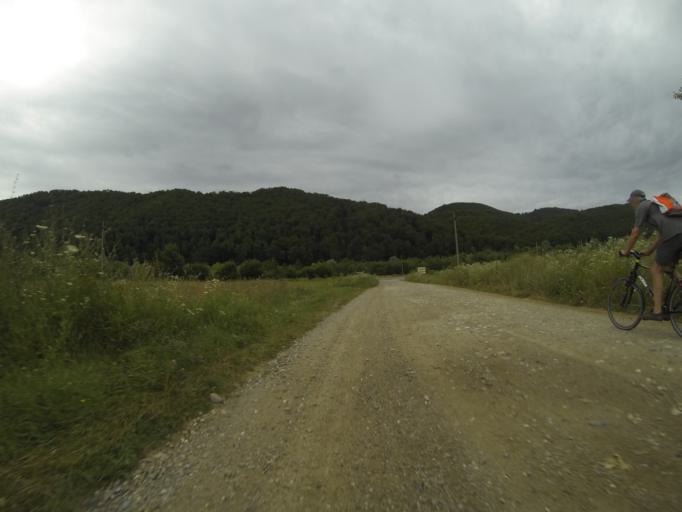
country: RO
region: Brasov
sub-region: Comuna Sinca Noua
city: Sinca Noua
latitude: 45.7362
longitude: 25.2286
